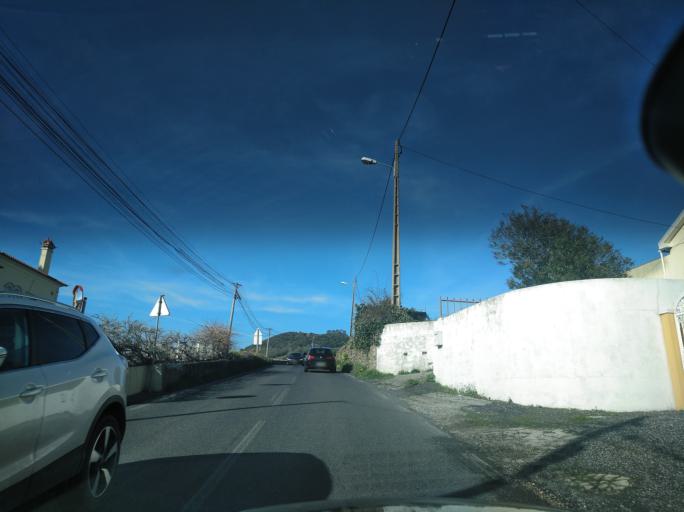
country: PT
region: Lisbon
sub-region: Sintra
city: Pero Pinheiro
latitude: 38.8906
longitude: -9.3269
